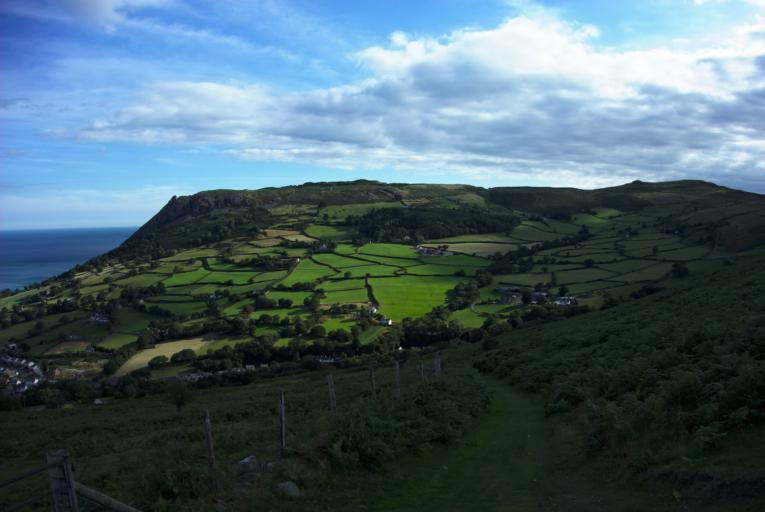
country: GB
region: Wales
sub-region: Conwy
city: Llanfairfechan
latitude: 53.2428
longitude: -3.9672
